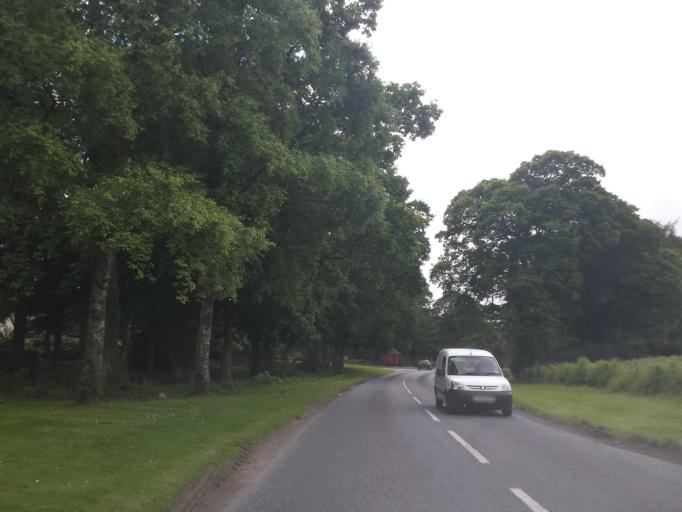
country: GB
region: Scotland
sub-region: Highland
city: Nairn
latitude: 57.5262
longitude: -3.9305
